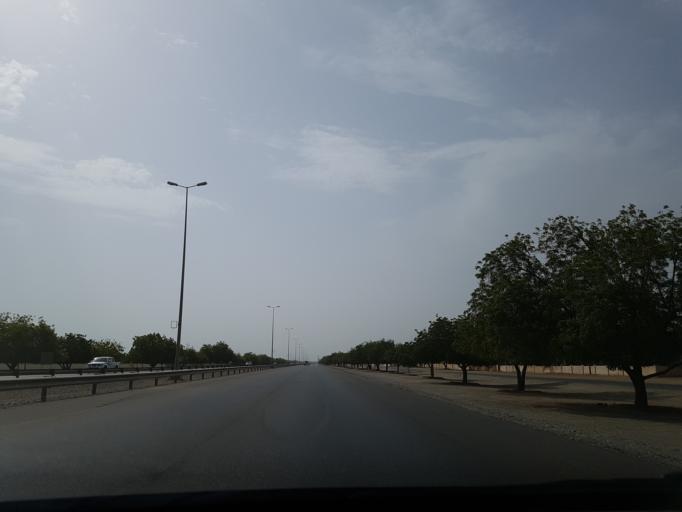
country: OM
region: Al Batinah
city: Saham
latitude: 24.1234
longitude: 56.9013
